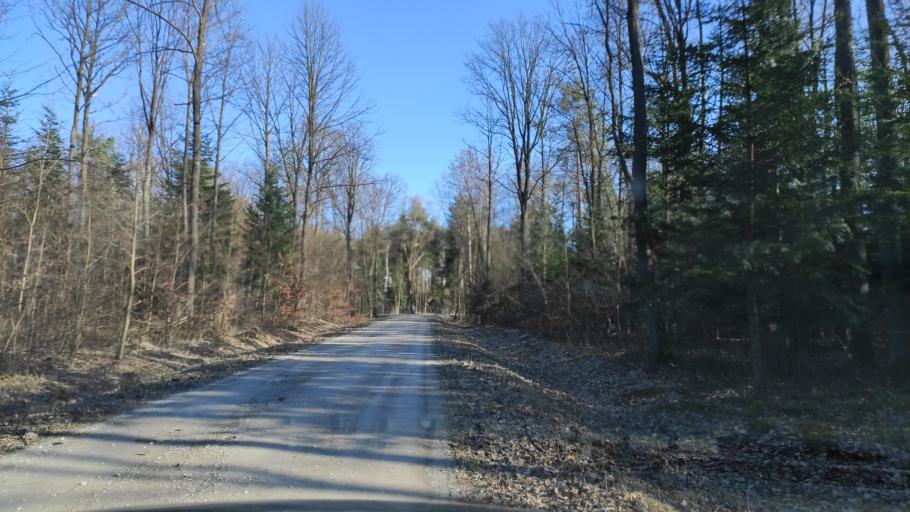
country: PL
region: Masovian Voivodeship
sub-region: Powiat radomski
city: Jedlnia-Letnisko
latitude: 51.4485
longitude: 21.2936
